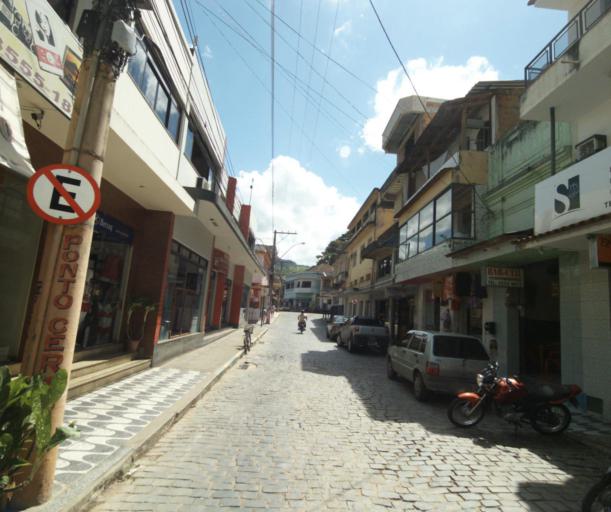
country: BR
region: Espirito Santo
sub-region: Mimoso Do Sul
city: Mimoso do Sul
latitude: -21.0618
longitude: -41.3641
